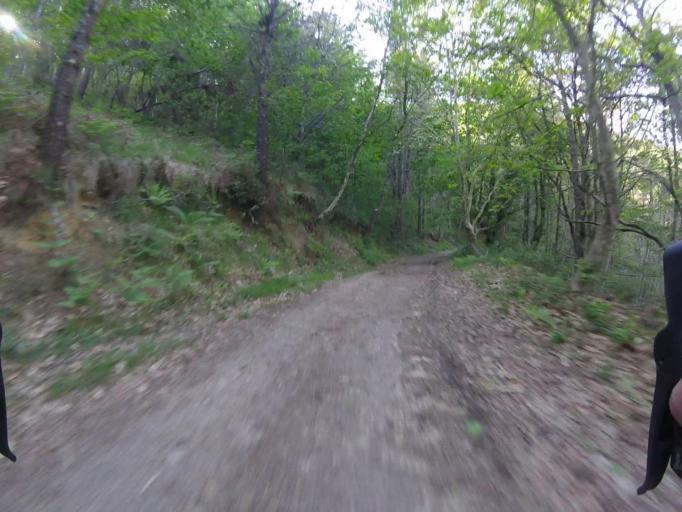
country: ES
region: Basque Country
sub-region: Provincia de Guipuzcoa
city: Fuenterrabia
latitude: 43.3553
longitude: -1.8309
